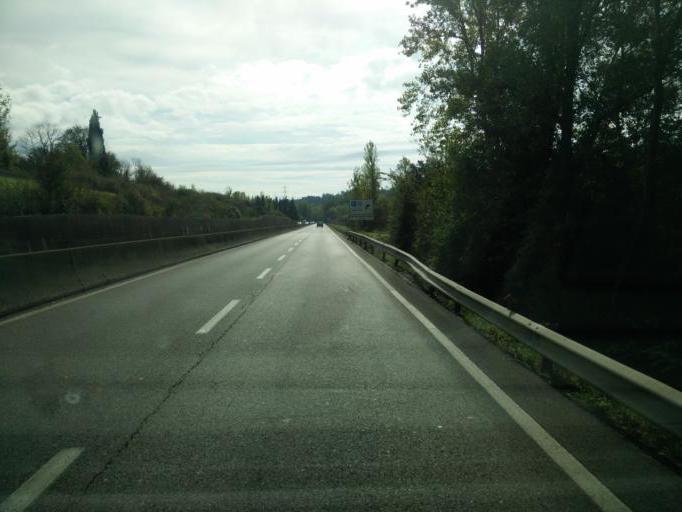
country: IT
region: Tuscany
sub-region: Provincia di Siena
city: Belverde
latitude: 43.3246
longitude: 11.2973
